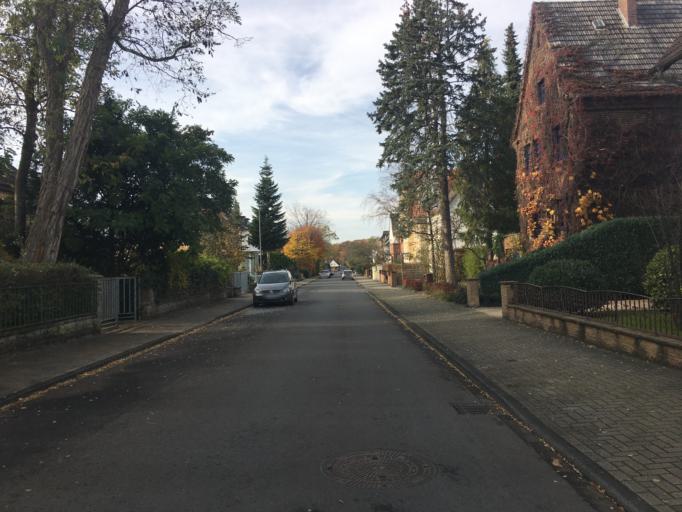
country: DE
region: North Rhine-Westphalia
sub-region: Regierungsbezirk Koln
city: Rath
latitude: 50.9525
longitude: 7.1022
